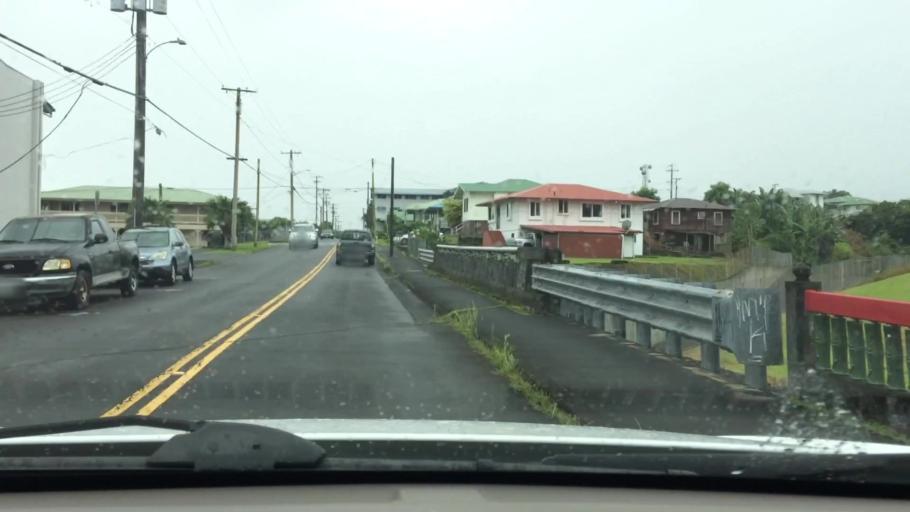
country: US
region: Hawaii
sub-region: Hawaii County
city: Hilo
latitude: 19.7191
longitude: -155.0868
